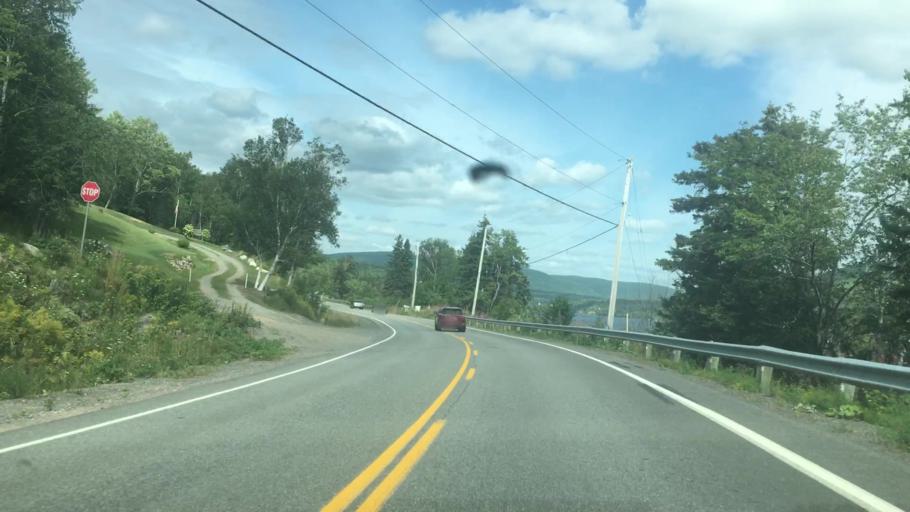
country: CA
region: Nova Scotia
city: Sydney Mines
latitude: 46.2723
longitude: -60.6096
